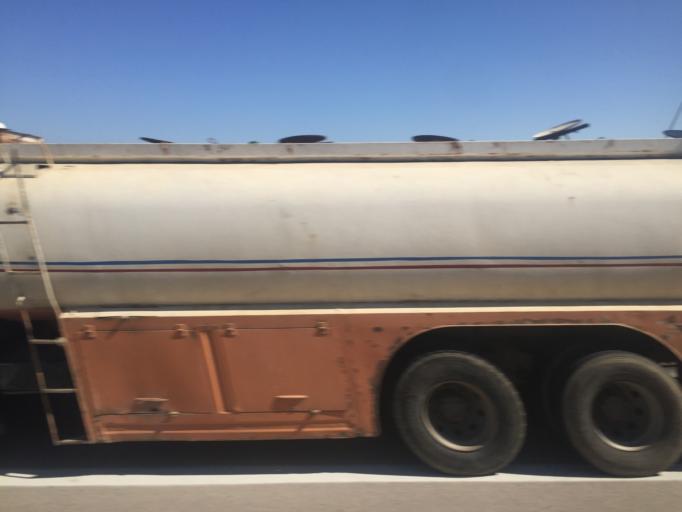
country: TR
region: Bursa
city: Mahmudiye
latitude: 40.2585
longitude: 28.6880
